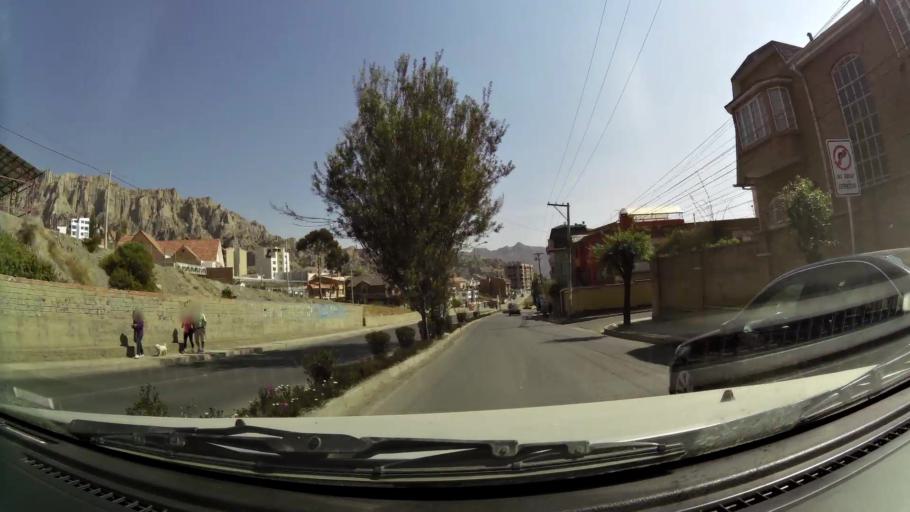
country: BO
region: La Paz
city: La Paz
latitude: -16.5470
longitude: -68.0729
